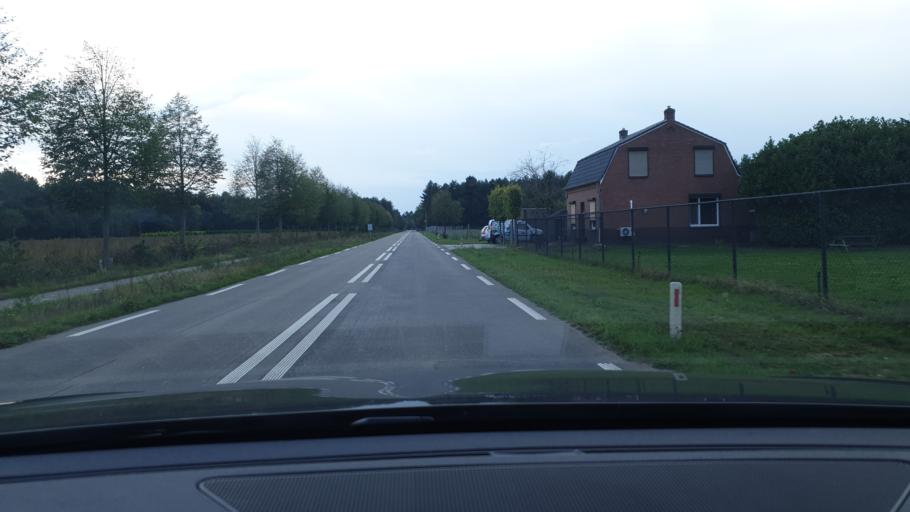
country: NL
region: Limburg
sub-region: Gemeente Venlo
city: Arcen
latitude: 51.4574
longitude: 6.1312
